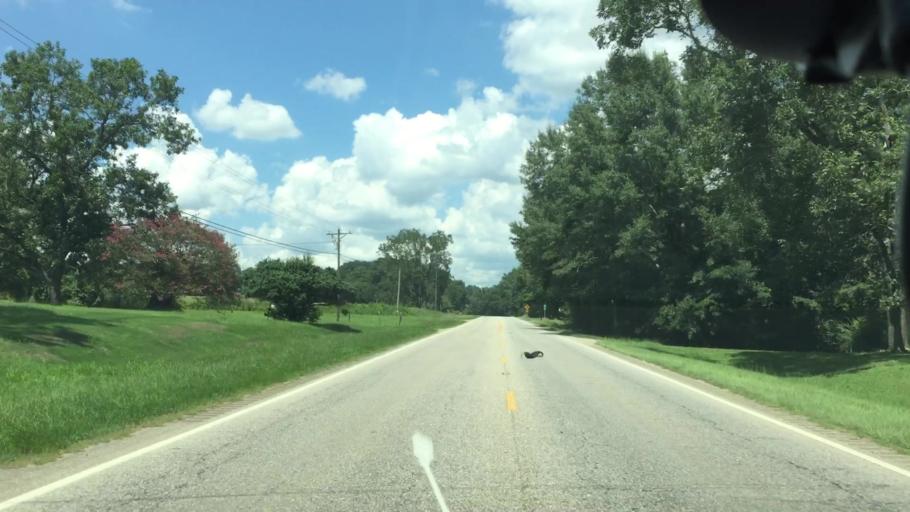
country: US
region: Alabama
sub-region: Pike County
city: Troy
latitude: 31.7342
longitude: -85.9574
